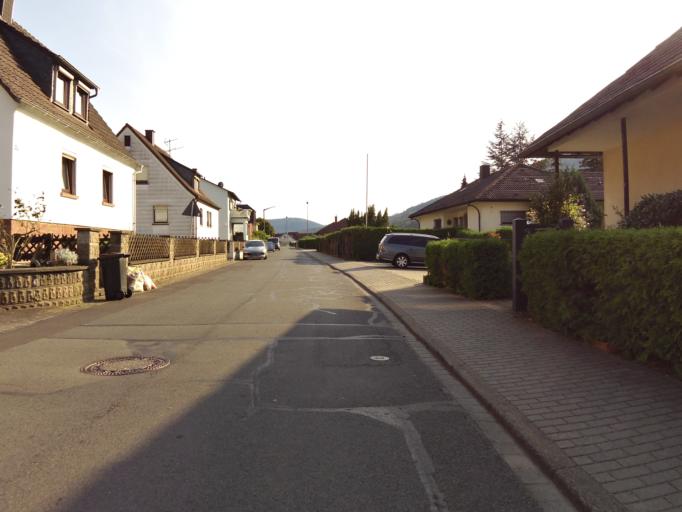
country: DE
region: Bavaria
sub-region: Regierungsbezirk Unterfranken
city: Weilbach
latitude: 49.6713
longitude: 9.2172
